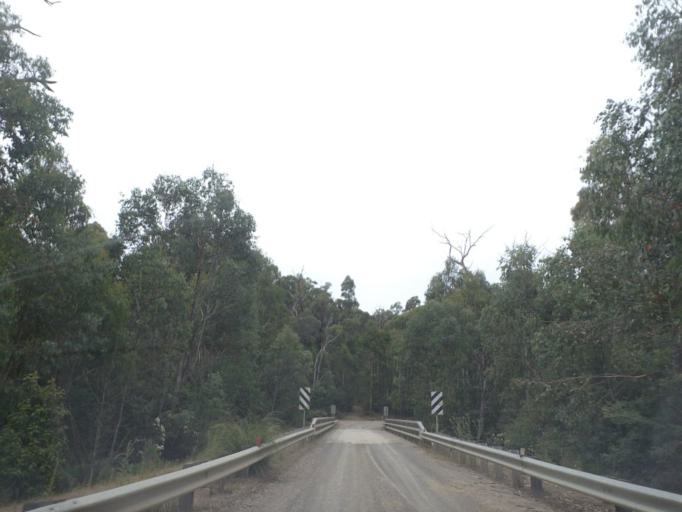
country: AU
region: Victoria
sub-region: Yarra Ranges
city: Healesville
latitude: -37.4245
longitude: 145.5688
